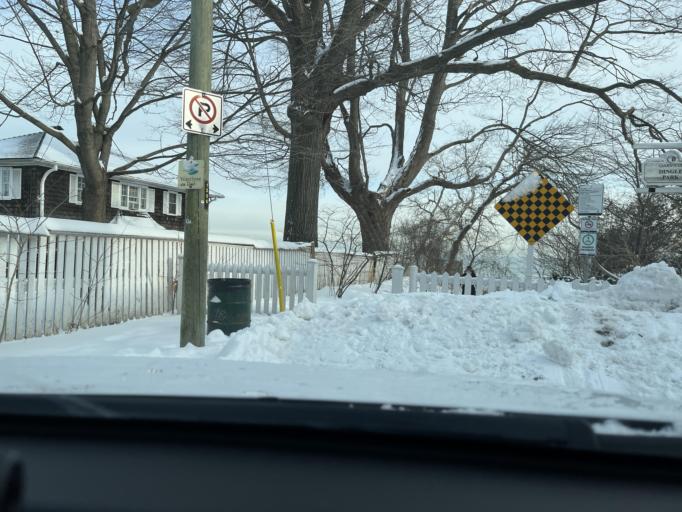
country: CA
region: Ontario
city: Oakville
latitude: 43.4474
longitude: -79.6620
